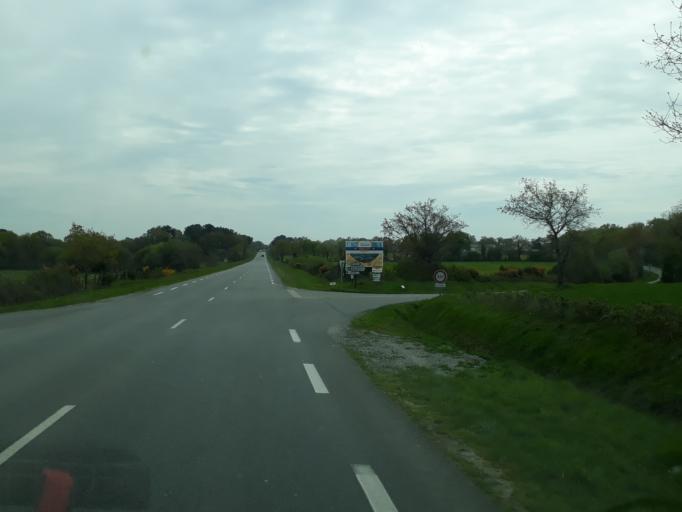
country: FR
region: Brittany
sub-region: Departement du Morbihan
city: Marzan
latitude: 47.5257
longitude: -2.3804
